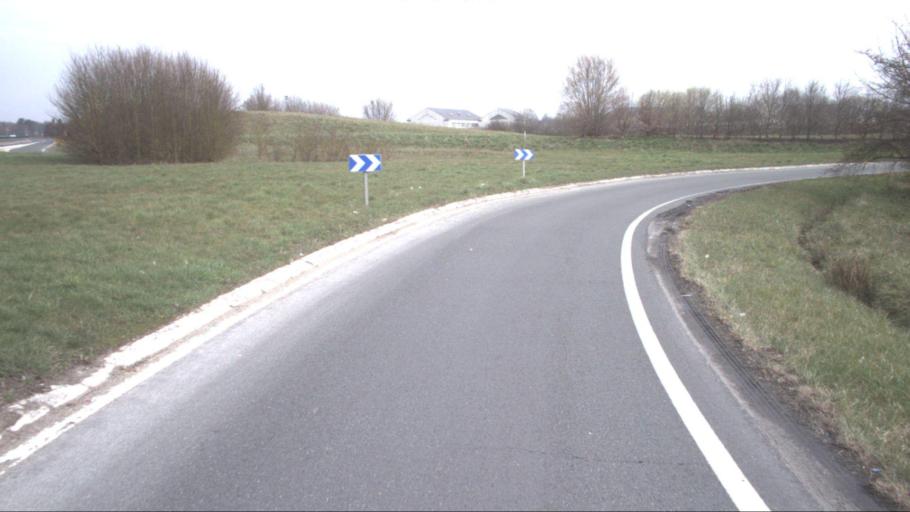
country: FR
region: Ile-de-France
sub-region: Departement des Yvelines
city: Rambouillet
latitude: 48.6457
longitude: 1.8430
